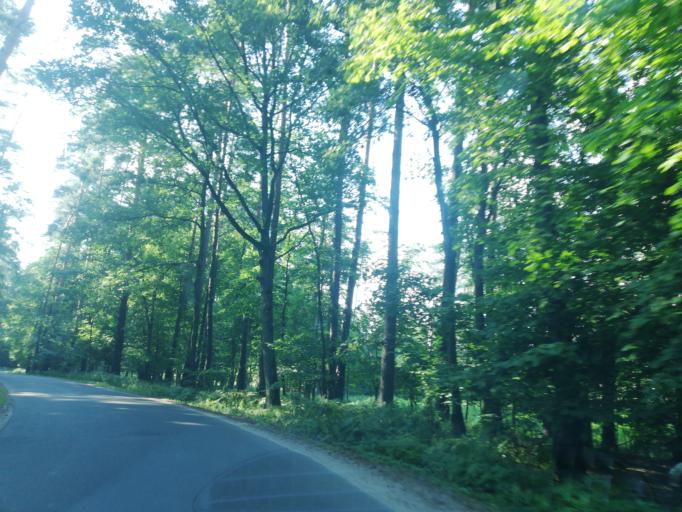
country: PL
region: Kujawsko-Pomorskie
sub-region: Powiat golubsko-dobrzynski
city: Ciechocin
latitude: 53.0794
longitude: 18.9500
